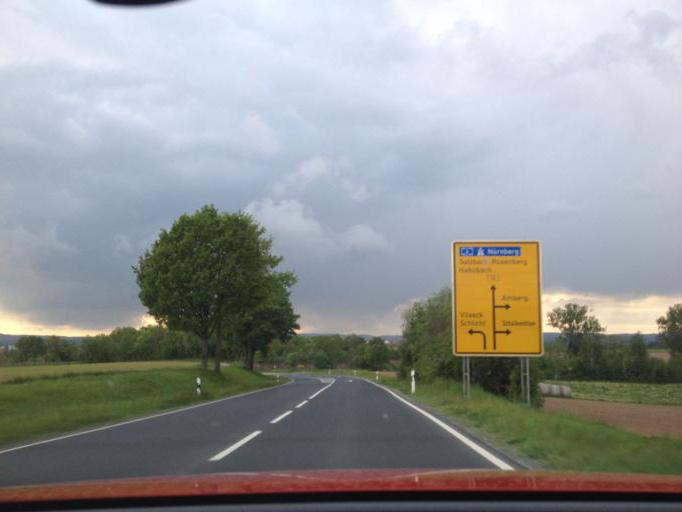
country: DE
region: Bavaria
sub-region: Upper Palatinate
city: Hahnbach
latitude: 49.5356
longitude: 11.8172
